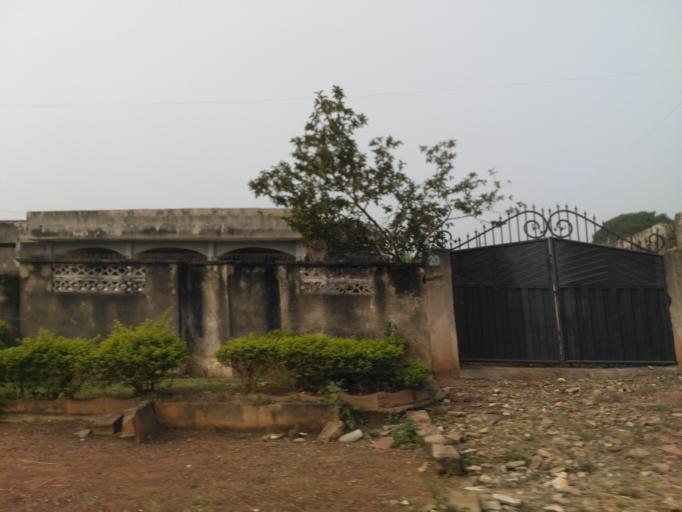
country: GH
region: Ashanti
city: Kumasi
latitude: 6.6522
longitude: -1.6284
